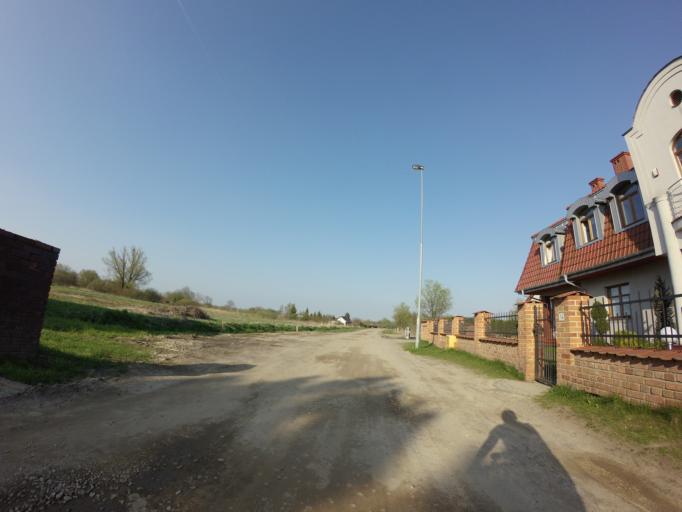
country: PL
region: West Pomeranian Voivodeship
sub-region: Powiat choszczenski
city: Choszczno
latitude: 53.1711
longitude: 15.4321
